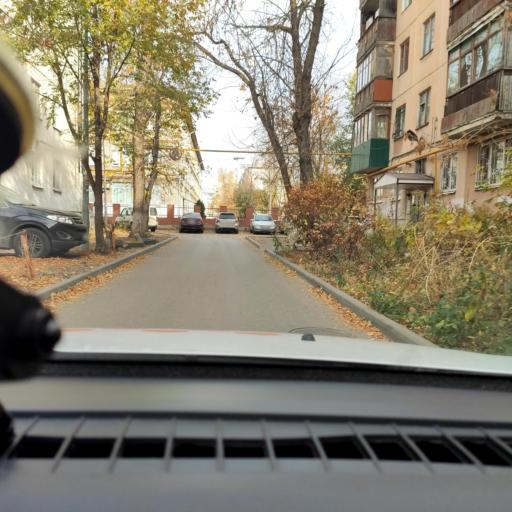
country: RU
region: Samara
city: Samara
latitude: 53.1886
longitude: 50.1838
